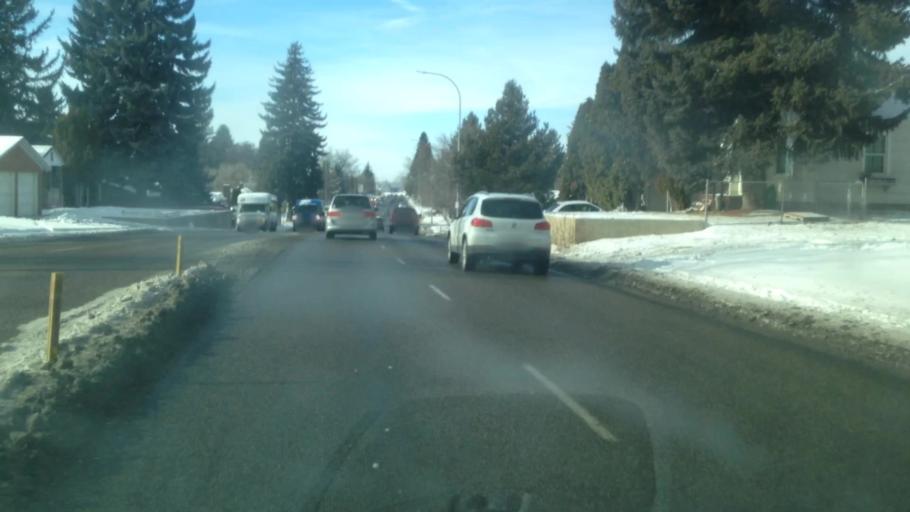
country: US
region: Idaho
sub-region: Bonneville County
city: Idaho Falls
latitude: 43.4826
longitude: -112.0343
